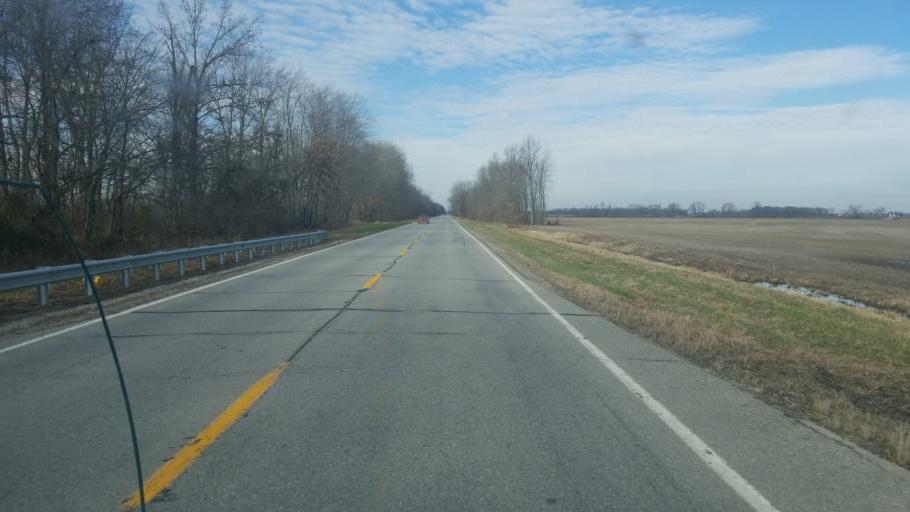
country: US
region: Illinois
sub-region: Saline County
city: Eldorado
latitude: 37.9424
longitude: -88.4640
